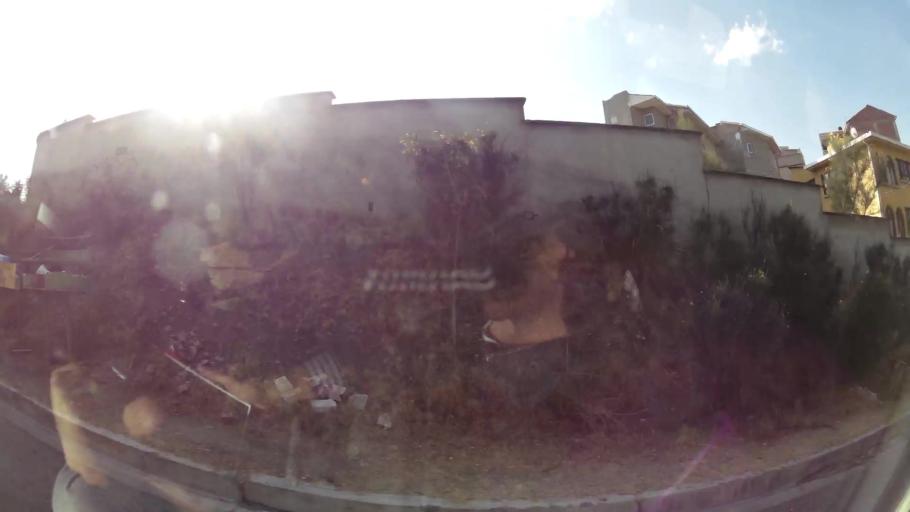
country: BO
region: La Paz
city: La Paz
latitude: -16.5313
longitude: -68.0774
